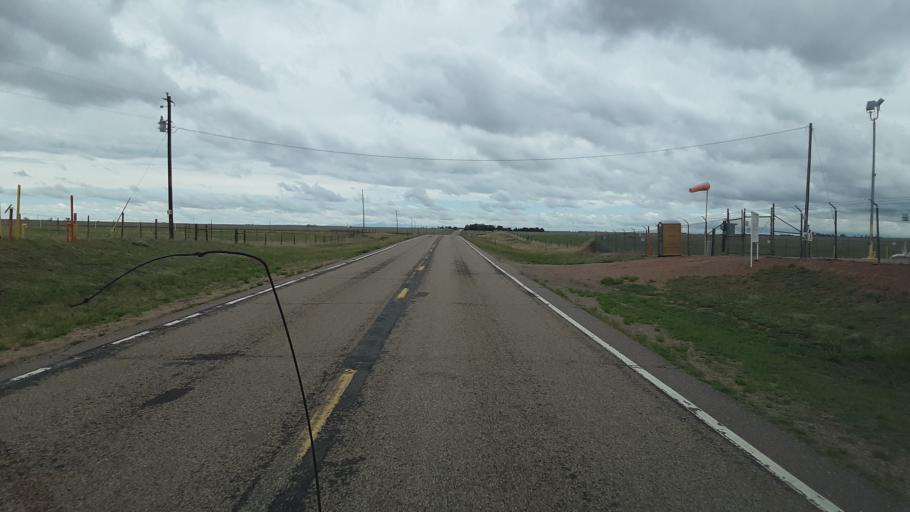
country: US
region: Colorado
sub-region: El Paso County
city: Ellicott
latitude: 38.8398
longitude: -104.0316
